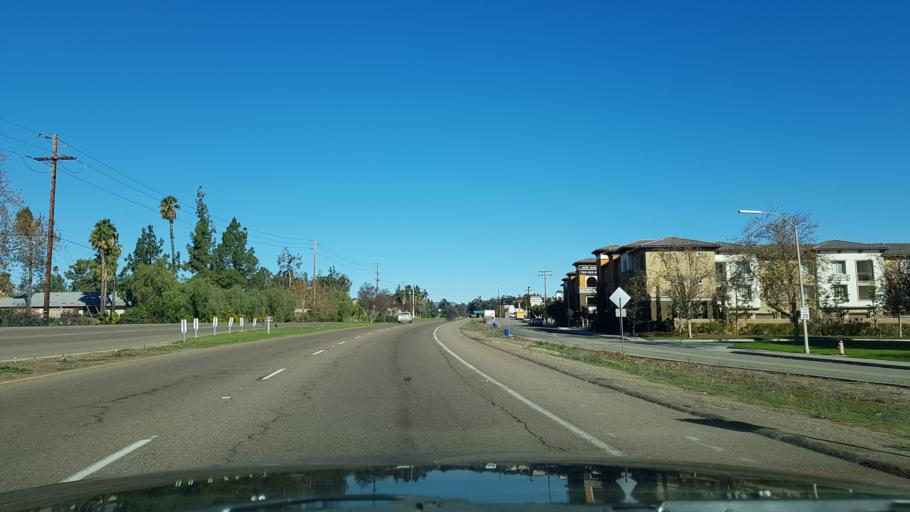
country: US
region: California
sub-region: San Diego County
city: Escondido
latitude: 33.0907
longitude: -117.0725
